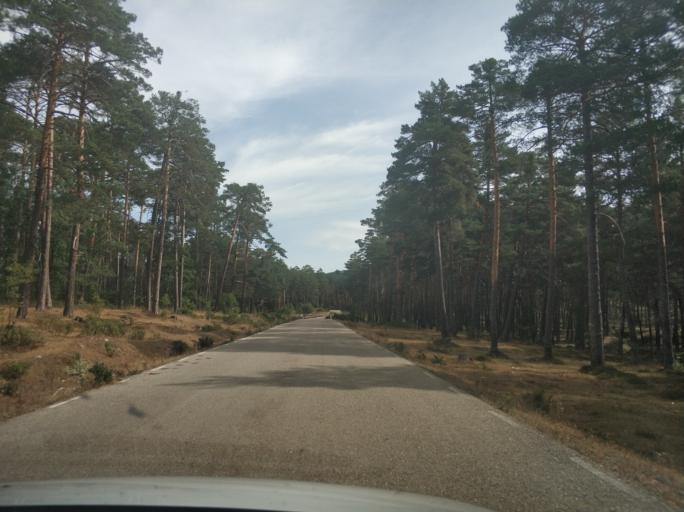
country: ES
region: Castille and Leon
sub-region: Provincia de Soria
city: Navaleno
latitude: 41.8712
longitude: -2.9414
